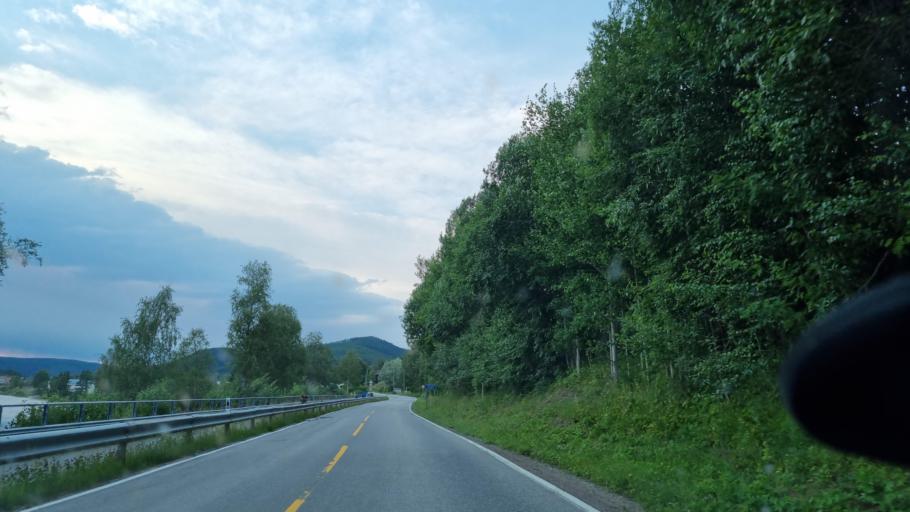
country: NO
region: Hedmark
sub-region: Trysil
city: Innbygda
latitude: 61.3070
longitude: 12.2730
